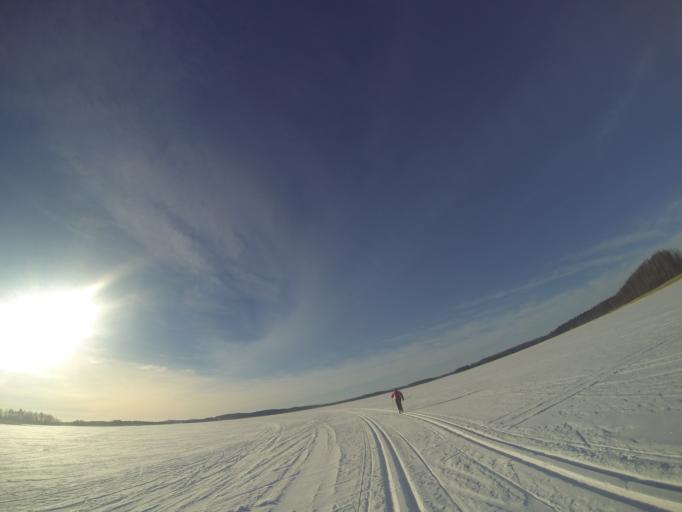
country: FI
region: Southern Savonia
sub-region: Savonlinna
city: Savonlinna
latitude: 61.8956
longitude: 28.9127
